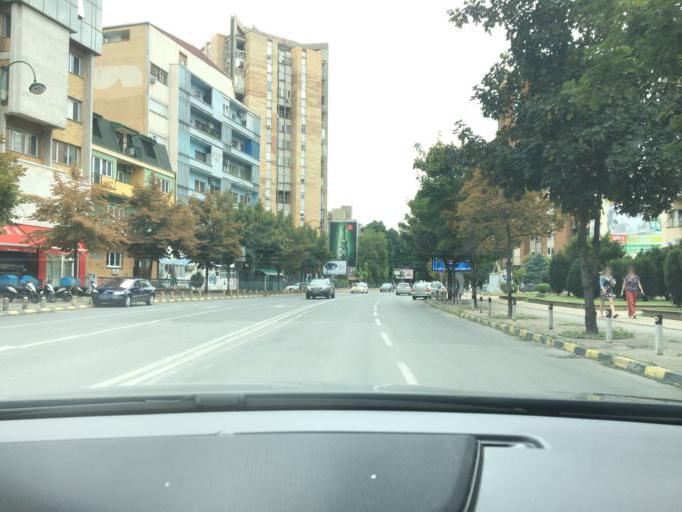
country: MK
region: Karpos
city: Skopje
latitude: 41.9953
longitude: 21.4252
